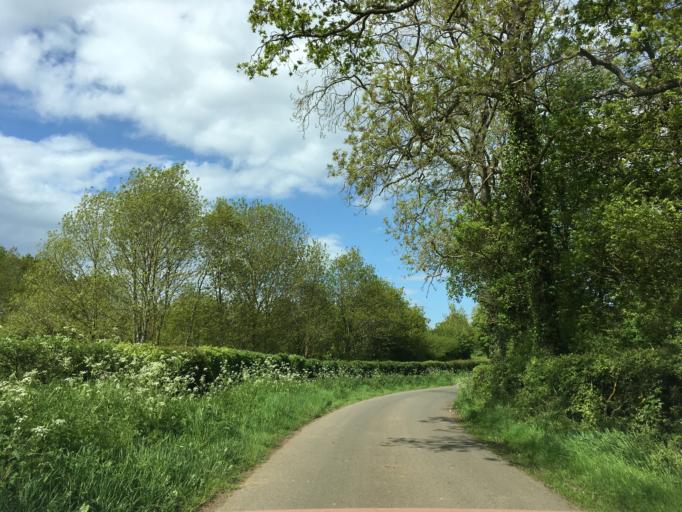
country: GB
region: England
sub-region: South Gloucestershire
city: Charfield
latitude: 51.6397
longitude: -2.3972
